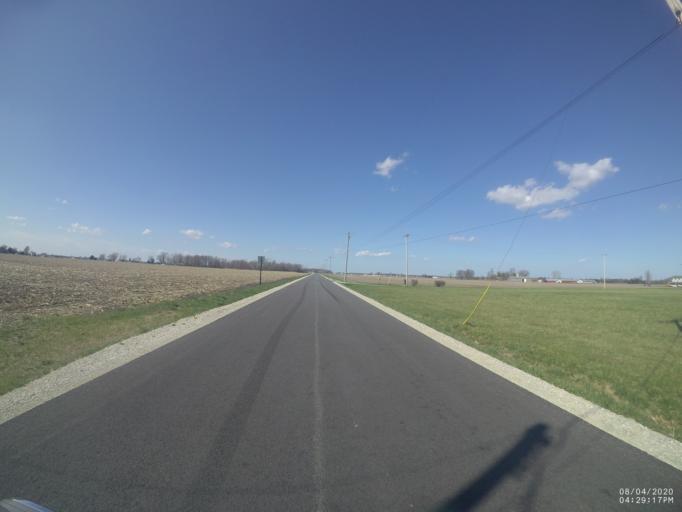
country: US
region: Ohio
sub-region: Sandusky County
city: Stony Prairie
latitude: 41.3371
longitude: -83.2042
